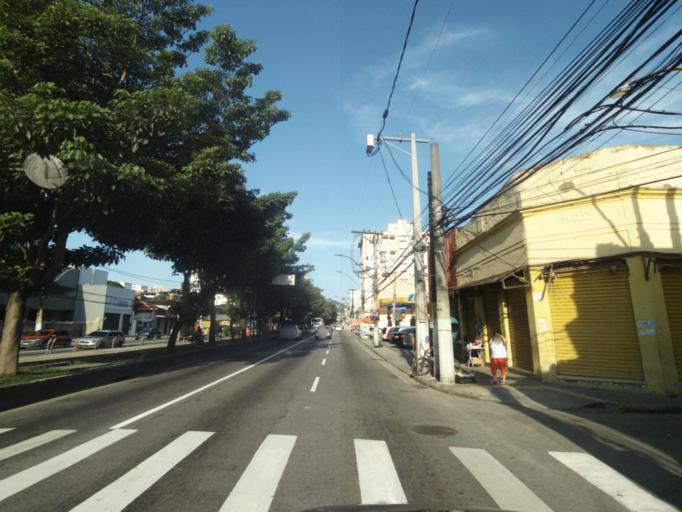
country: BR
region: Rio de Janeiro
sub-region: Niteroi
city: Niteroi
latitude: -22.8813
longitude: -43.0891
